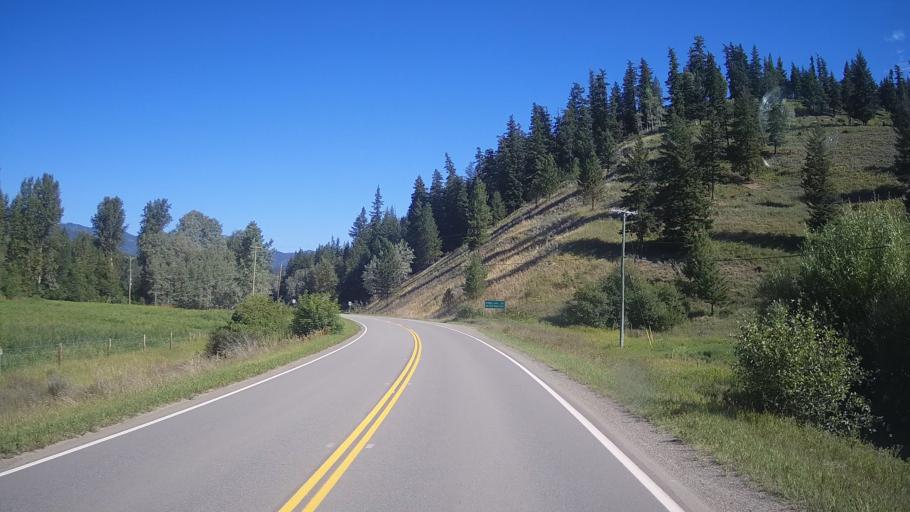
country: CA
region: British Columbia
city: Kamloops
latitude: 51.4354
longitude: -120.2079
